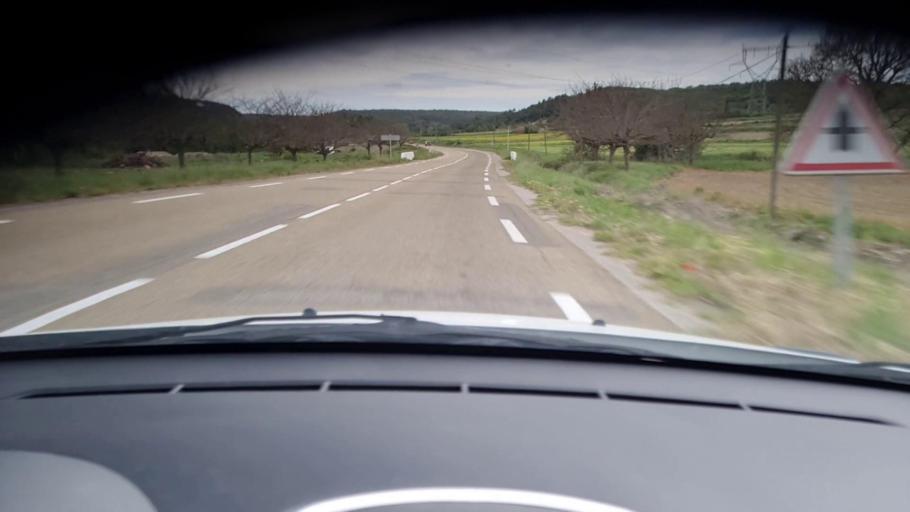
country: FR
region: Languedoc-Roussillon
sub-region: Departement du Gard
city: Blauzac
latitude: 43.9560
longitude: 4.3817
